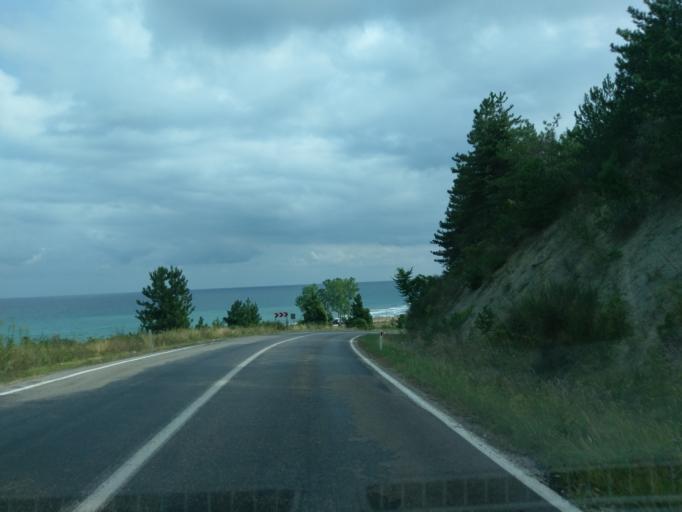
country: TR
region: Sinop
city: Yenikonak
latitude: 41.9407
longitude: 34.7152
